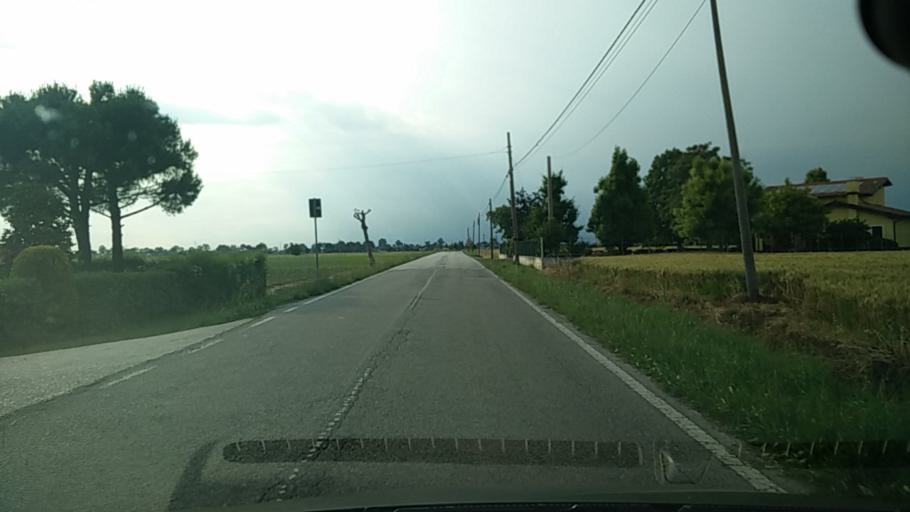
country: IT
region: Veneto
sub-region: Provincia di Venezia
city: Passarella
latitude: 45.5827
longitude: 12.6039
